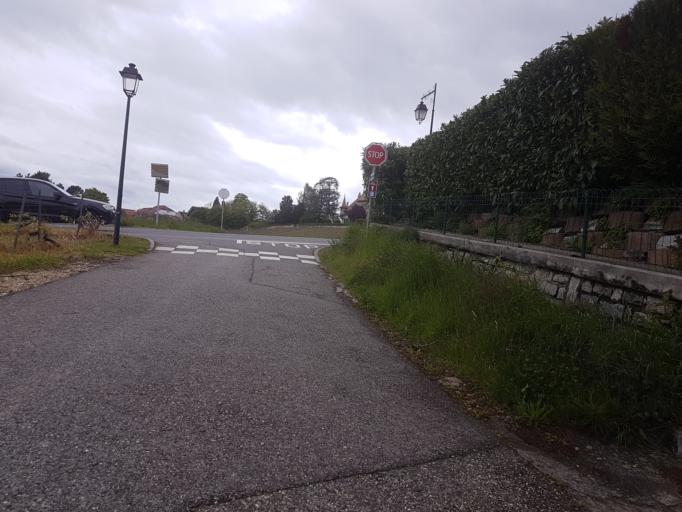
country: CH
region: Vaud
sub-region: Ouest Lausannois District
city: Bussigny
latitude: 46.5370
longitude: 6.5447
